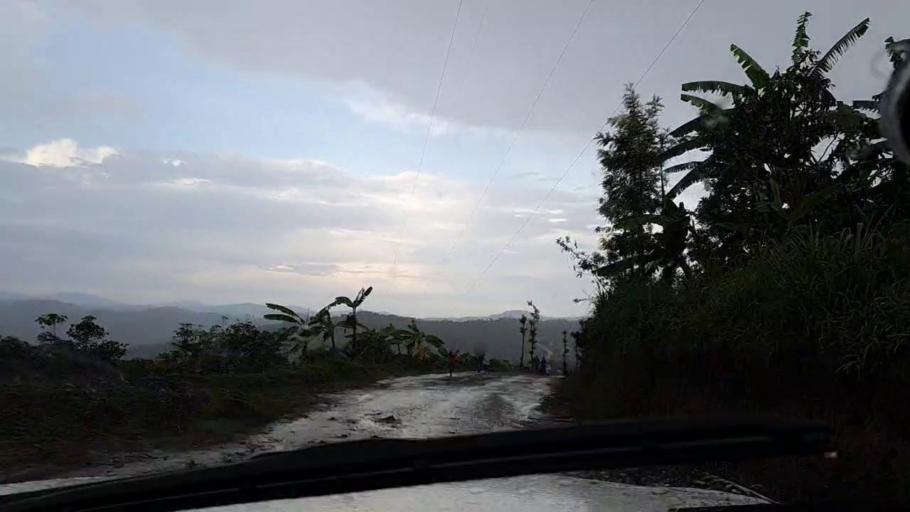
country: BI
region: Kayanza
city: Kayanza
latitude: -2.7756
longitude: 29.5399
